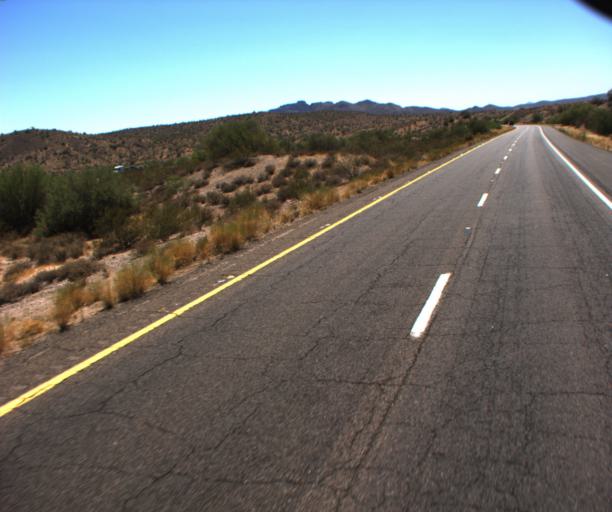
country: US
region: Arizona
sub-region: Maricopa County
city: Fountain Hills
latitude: 33.5832
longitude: -111.6166
